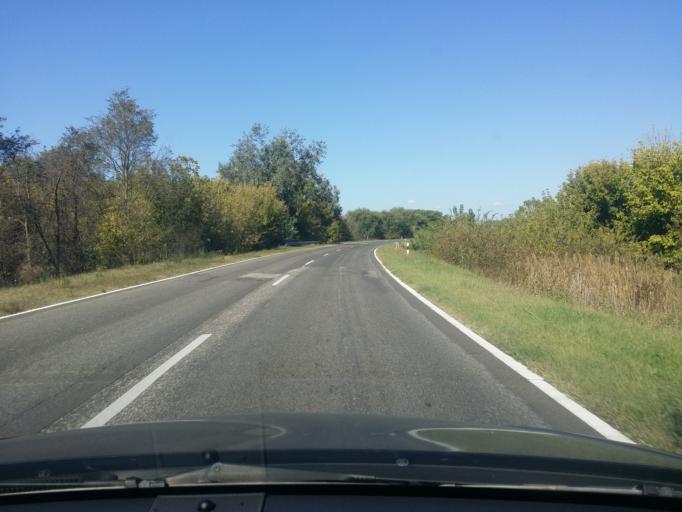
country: HU
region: Csongrad
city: Pusztaszer
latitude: 46.5633
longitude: 19.9405
